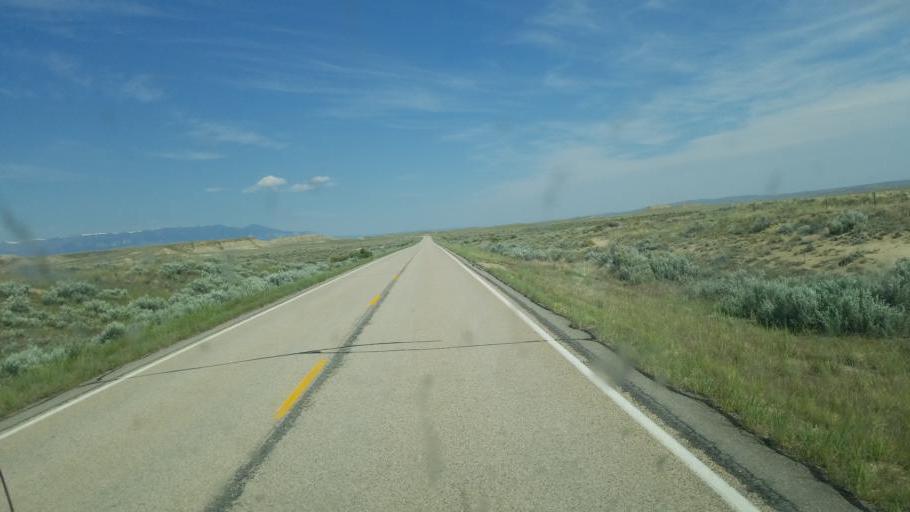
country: US
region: Wyoming
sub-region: Park County
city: Powell
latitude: 44.8240
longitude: -108.9755
